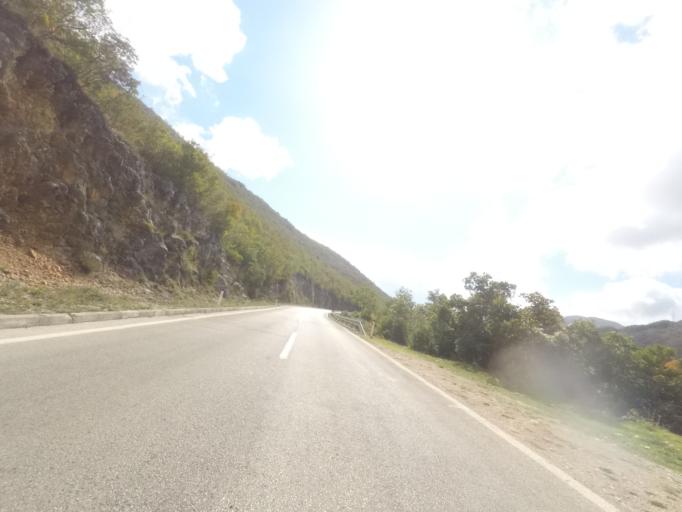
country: BA
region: Republika Srpska
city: Trebinje
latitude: 42.5988
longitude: 18.4289
